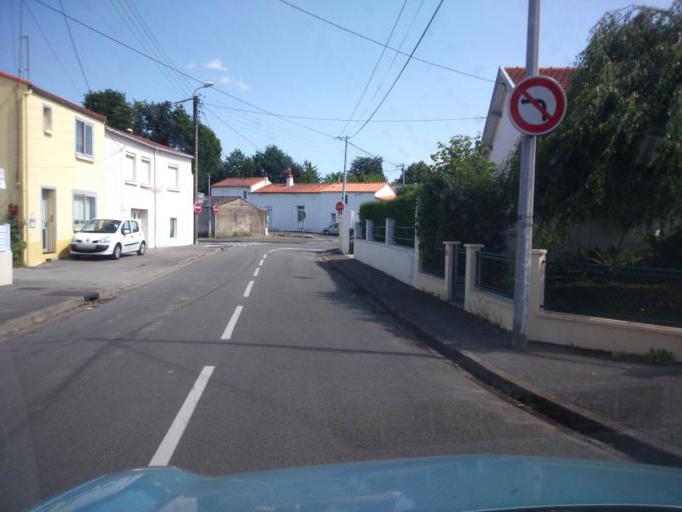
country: FR
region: Pays de la Loire
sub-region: Departement de la Loire-Atlantique
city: Saint-Sebastien-sur-Loire
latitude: 47.1952
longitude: -1.5178
